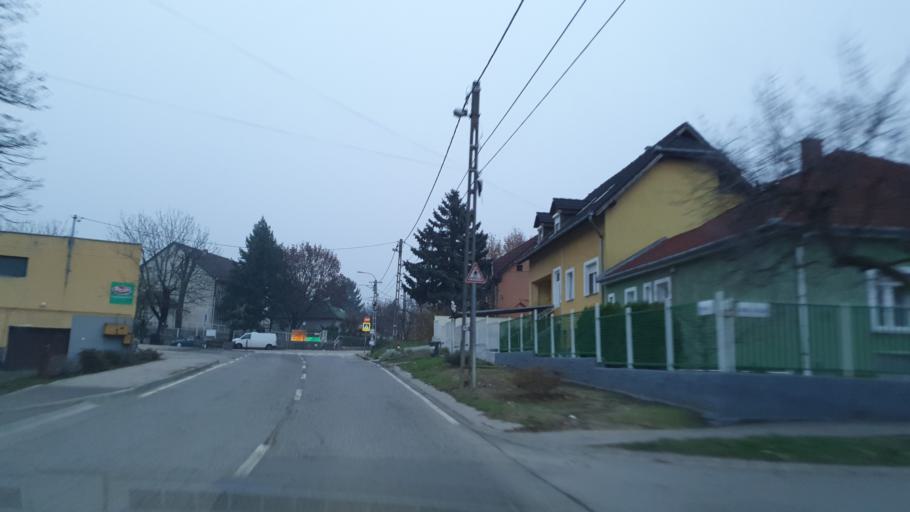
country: HU
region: Pest
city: Csomor
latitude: 47.5427
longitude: 19.2243
